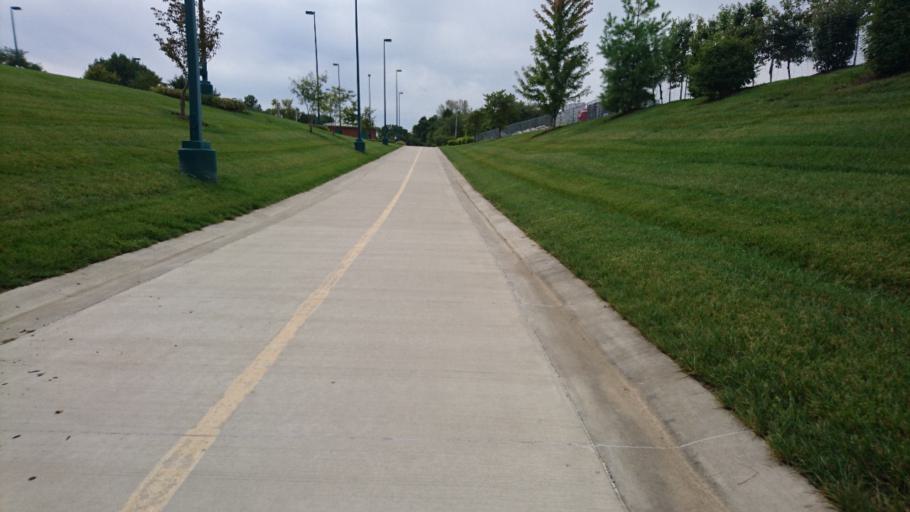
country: US
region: Illinois
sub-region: Madison County
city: Edwardsville
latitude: 38.8050
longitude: -89.9516
